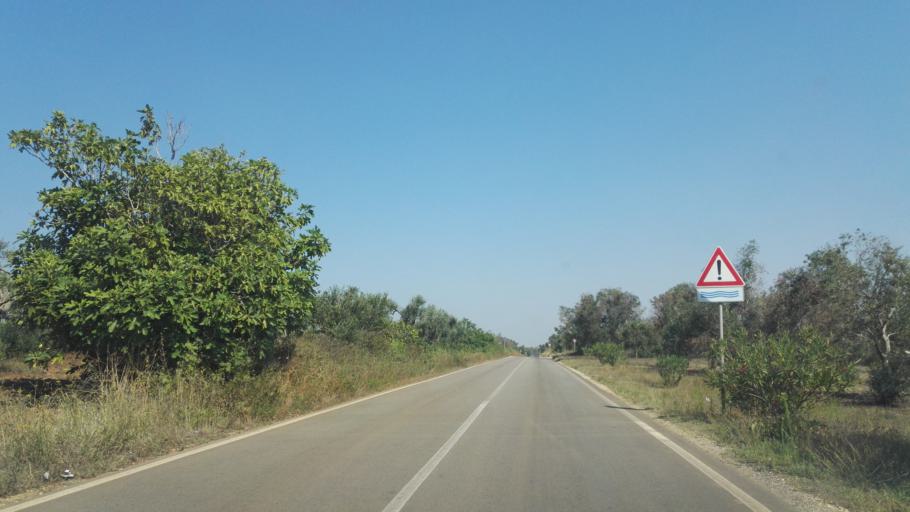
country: IT
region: Apulia
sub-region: Provincia di Lecce
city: Nardo
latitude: 40.1852
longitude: 17.9714
